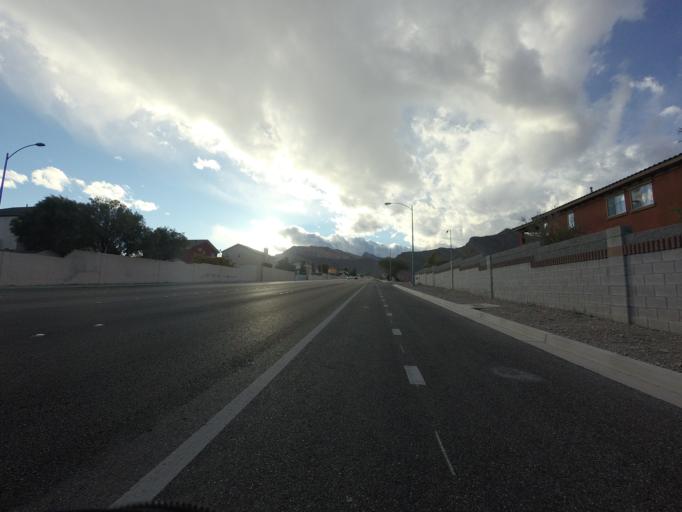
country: US
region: Nevada
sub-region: Clark County
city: Summerlin South
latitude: 36.2337
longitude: -115.3015
